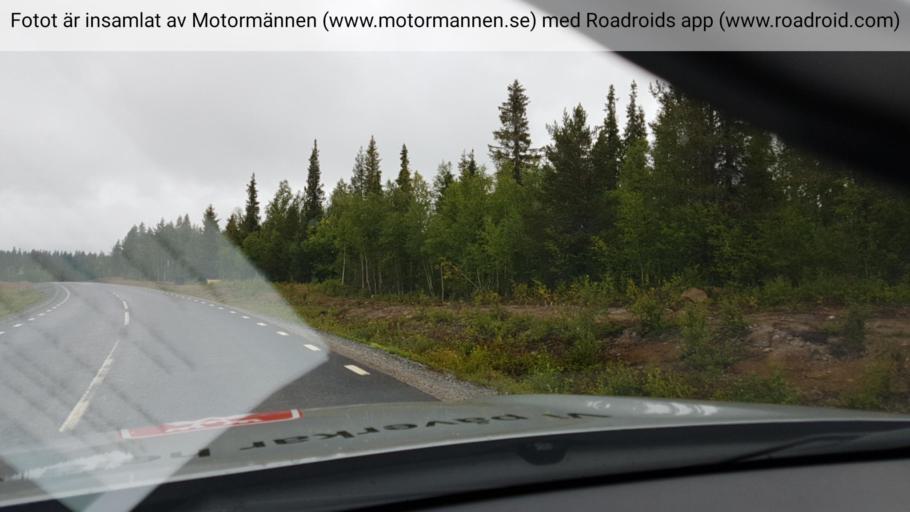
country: SE
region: Norrbotten
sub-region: Gallivare Kommun
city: Gaellivare
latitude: 66.8367
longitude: 21.0412
